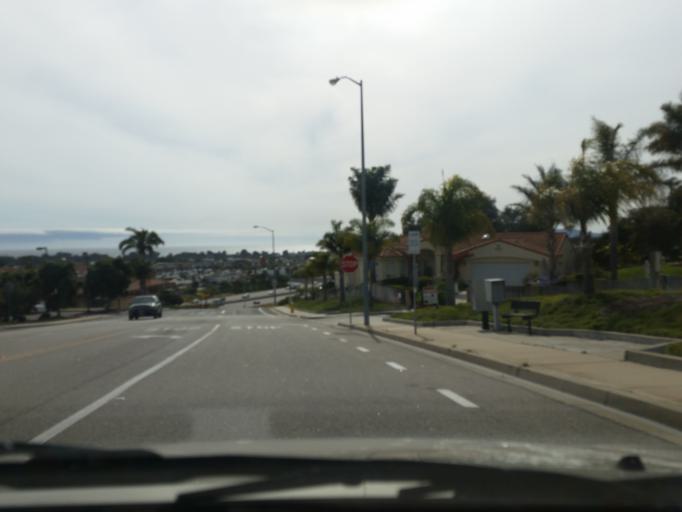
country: US
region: California
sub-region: San Luis Obispo County
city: Grover Beach
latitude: 35.1375
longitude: -120.6212
